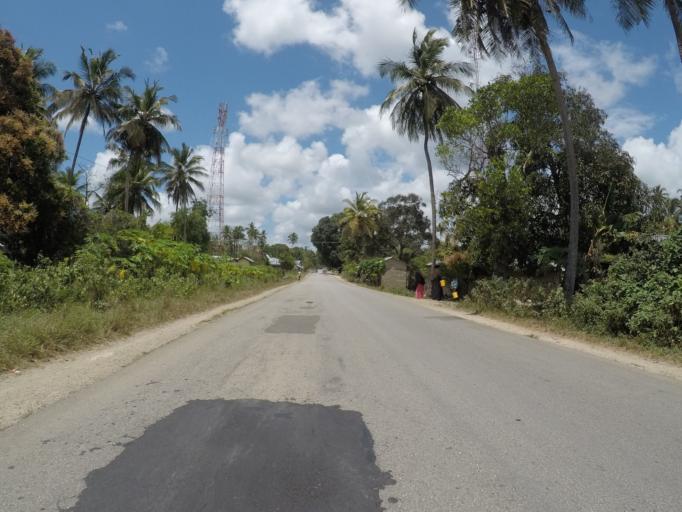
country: TZ
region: Zanzibar Central/South
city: Nganane
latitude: -6.2869
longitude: 39.4373
